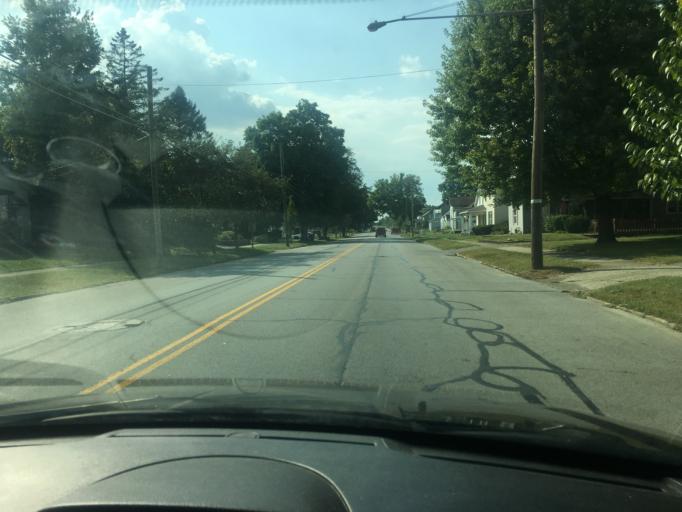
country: US
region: Ohio
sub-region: Champaign County
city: Urbana
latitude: 40.1090
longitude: -83.7662
